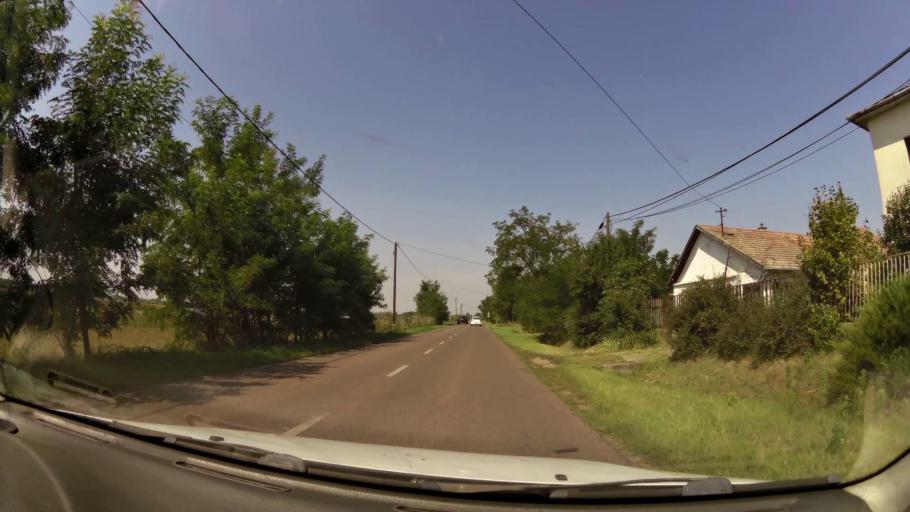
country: HU
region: Pest
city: Tapiobicske
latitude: 47.3719
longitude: 19.6759
